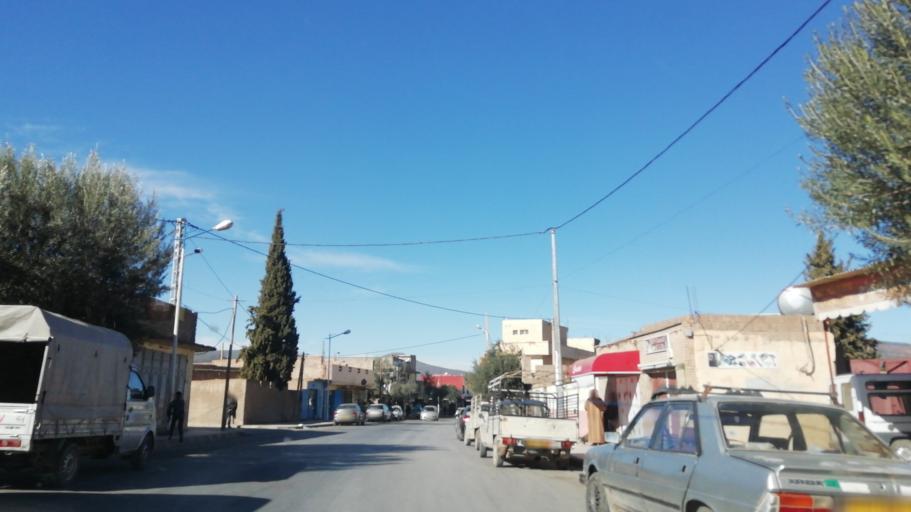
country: DZ
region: Tlemcen
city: Sebdou
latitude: 34.6479
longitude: -1.3227
